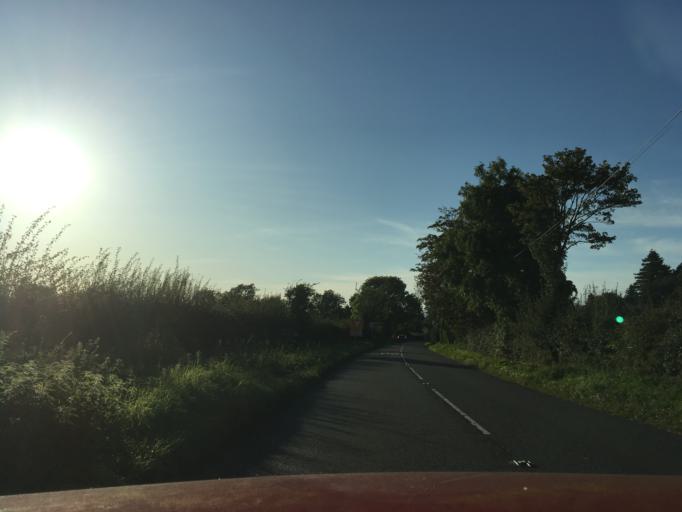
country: GB
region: England
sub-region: Worcestershire
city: Bredon
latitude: 52.0145
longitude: -2.1283
